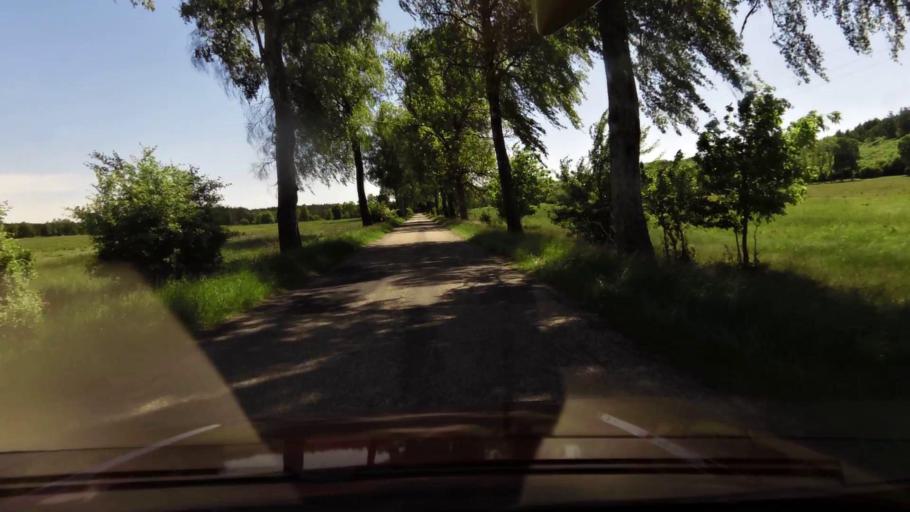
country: PL
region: West Pomeranian Voivodeship
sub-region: Powiat koszalinski
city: Bobolice
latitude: 54.0379
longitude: 16.6044
